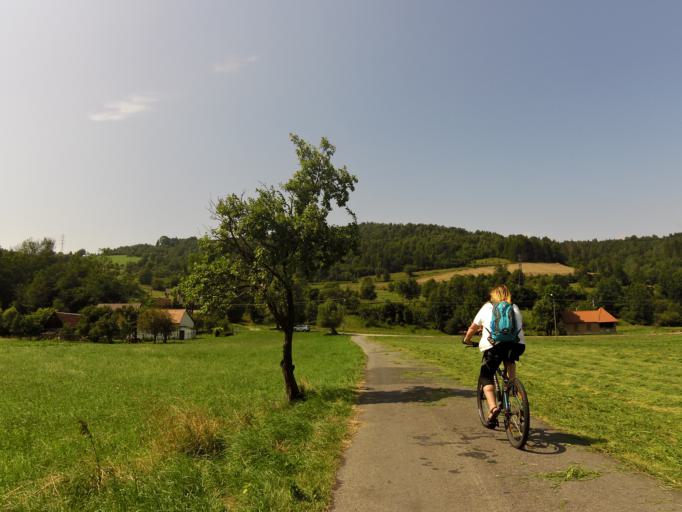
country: PL
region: Silesian Voivodeship
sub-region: Powiat zywiecki
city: Milowka
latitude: 49.5739
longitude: 19.0901
